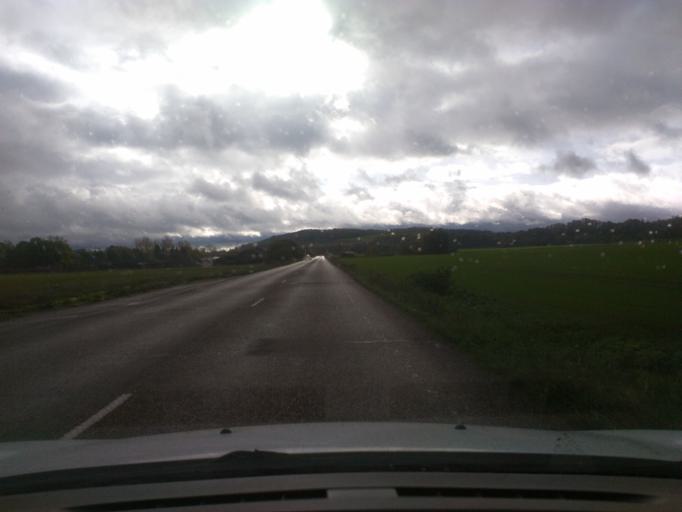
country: FR
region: Lorraine
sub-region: Departement des Vosges
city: Charmes
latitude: 48.3849
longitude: 6.2640
